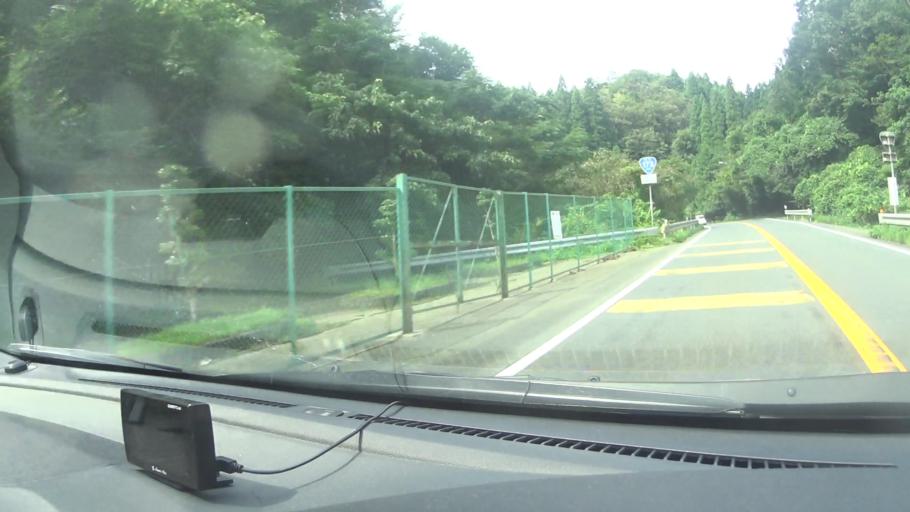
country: JP
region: Hyogo
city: Sasayama
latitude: 35.1435
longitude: 135.3419
